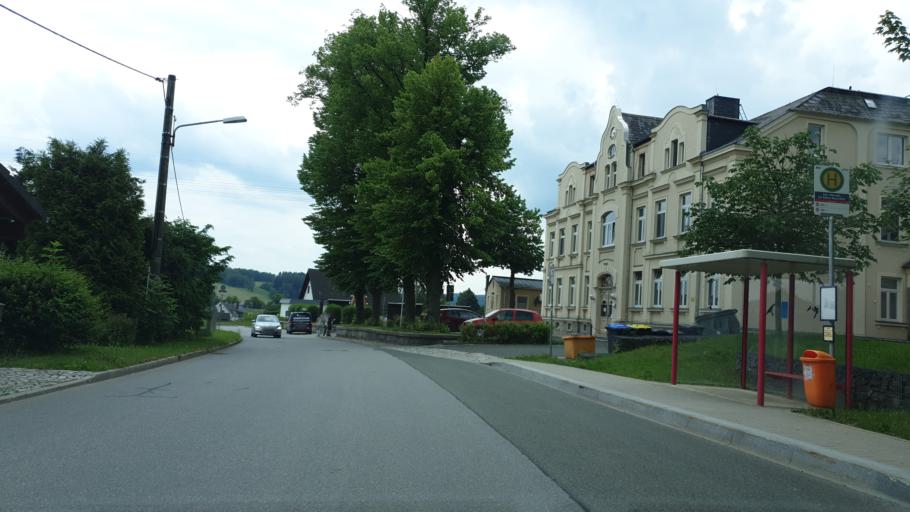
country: DE
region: Saxony
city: Lossnitz
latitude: 50.6175
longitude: 12.7090
